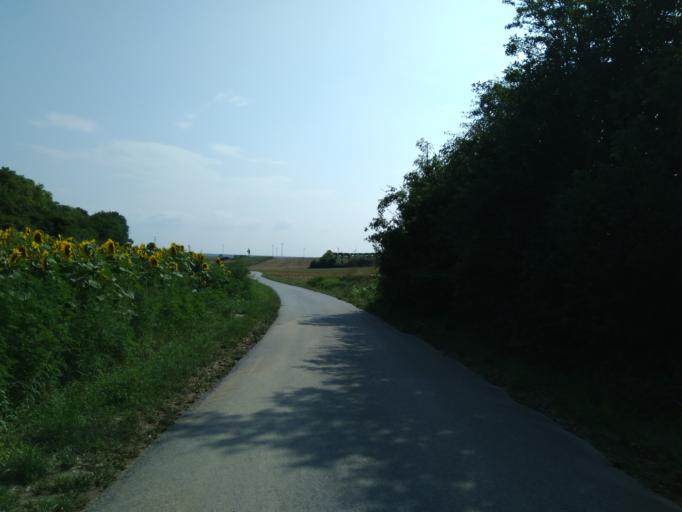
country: AT
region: Lower Austria
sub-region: Politischer Bezirk Ganserndorf
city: Auersthal
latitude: 48.3880
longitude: 16.6774
